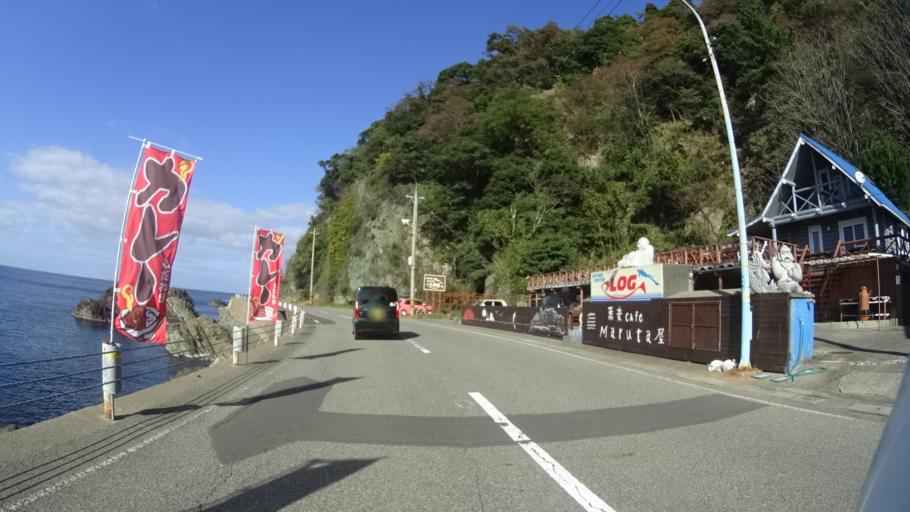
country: JP
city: Asahi
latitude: 35.9572
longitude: 135.9775
